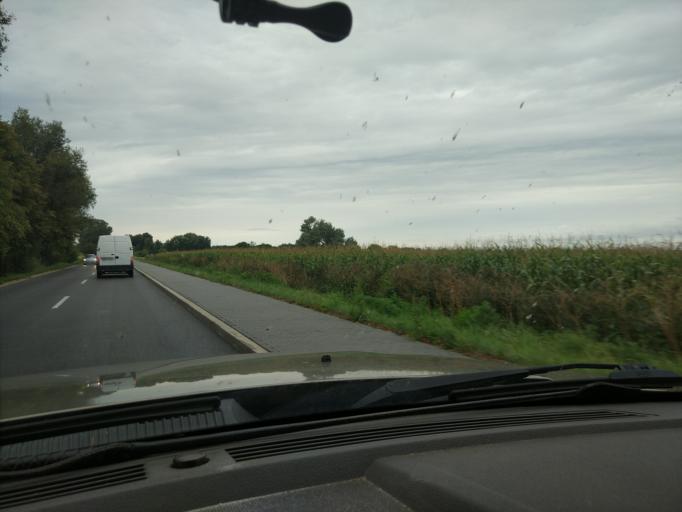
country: PL
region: Masovian Voivodeship
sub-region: Powiat pruszkowski
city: Brwinow
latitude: 52.1596
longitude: 20.7337
